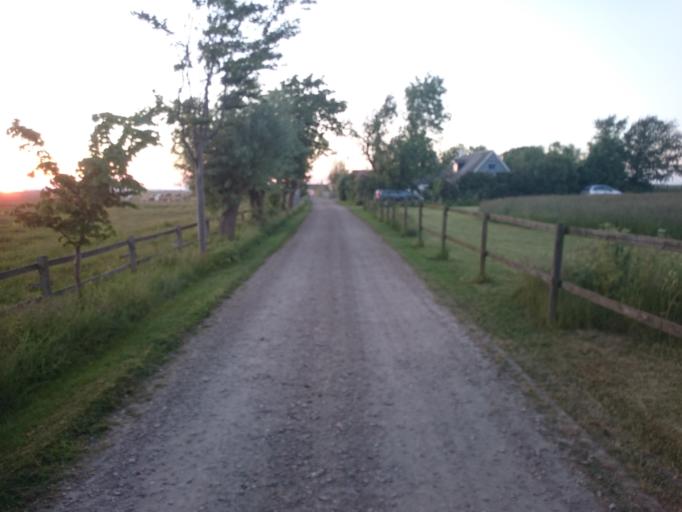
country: SE
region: Skane
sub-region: Malmo
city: Tygelsjo
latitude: 55.4779
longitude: 12.9611
